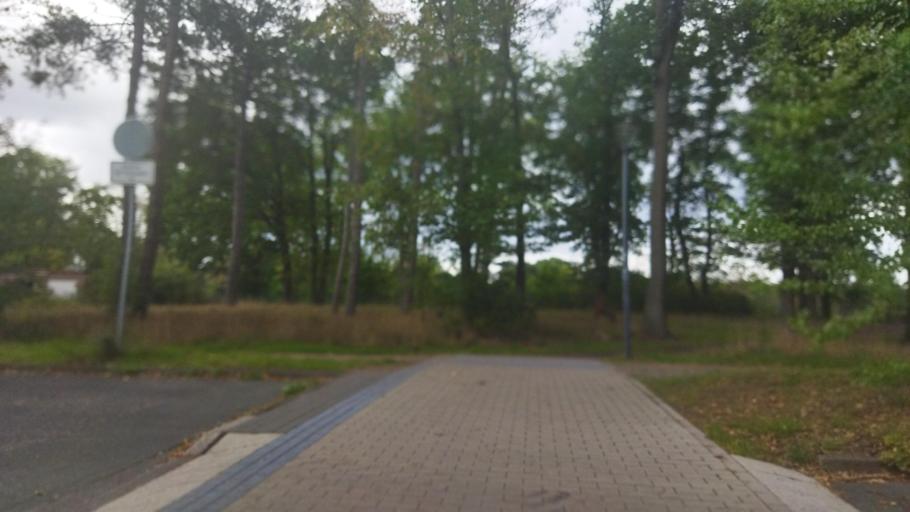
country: DE
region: North Rhine-Westphalia
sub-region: Regierungsbezirk Munster
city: Haltern
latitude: 51.7429
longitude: 7.2024
